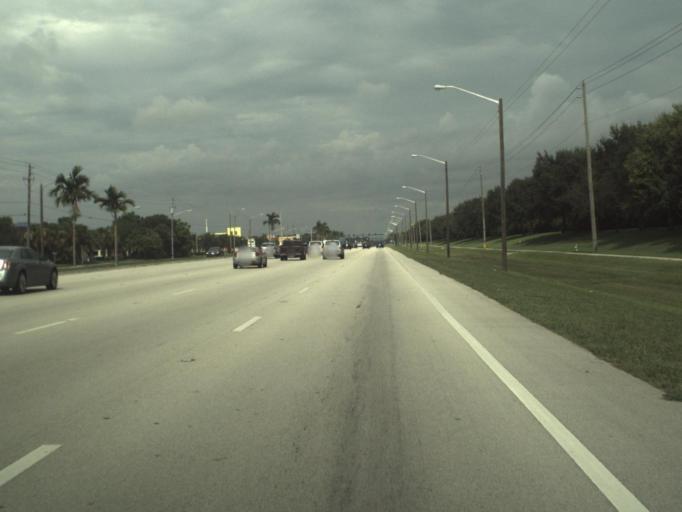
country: US
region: Florida
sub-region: Palm Beach County
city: Plantation Mobile Home Park
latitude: 26.7084
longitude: -80.1605
